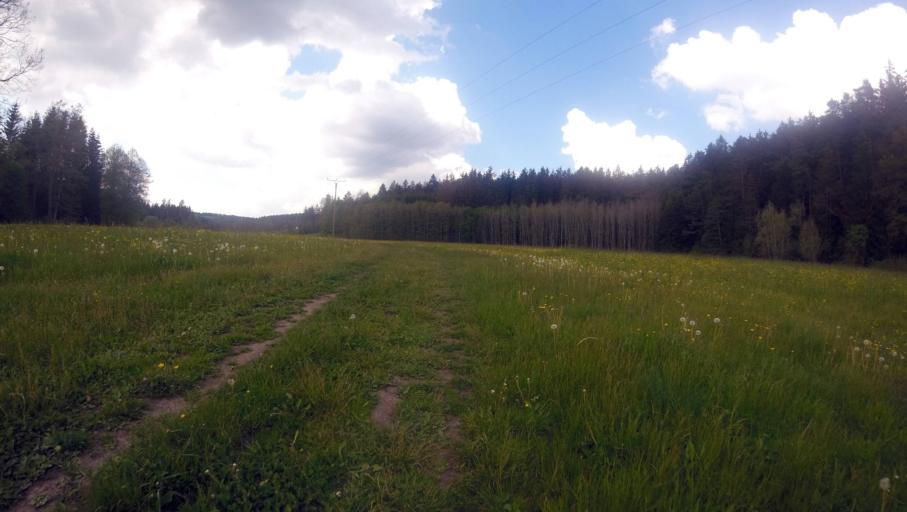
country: DE
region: Baden-Wuerttemberg
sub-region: Regierungsbezirk Stuttgart
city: Spraitbach
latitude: 48.8628
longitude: 9.7549
